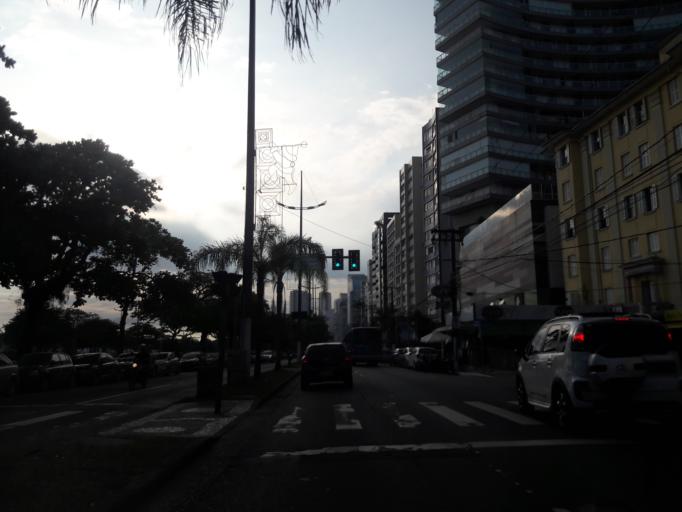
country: BR
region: Sao Paulo
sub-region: Santos
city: Santos
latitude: -23.9680
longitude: -46.3421
